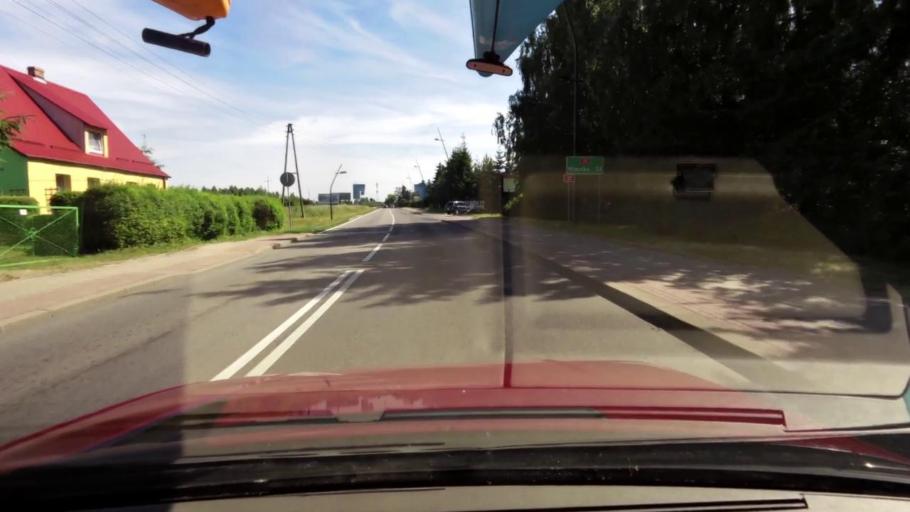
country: PL
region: Pomeranian Voivodeship
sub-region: Powiat slupski
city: Kobylnica
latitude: 54.4375
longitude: 16.9973
